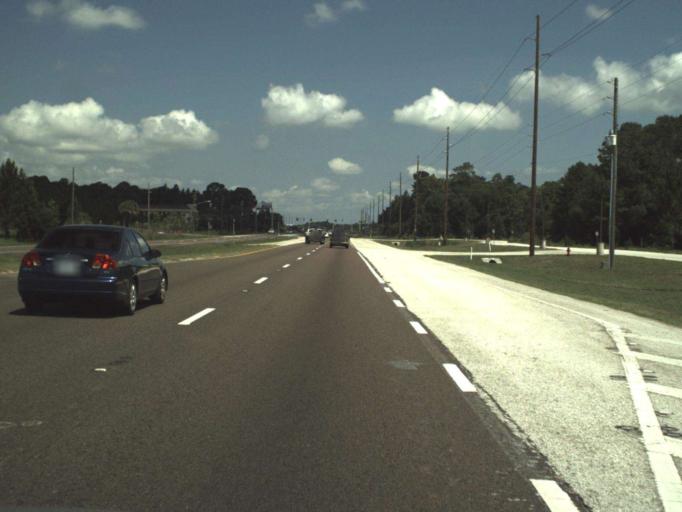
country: US
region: Florida
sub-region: Lake County
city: Mount Dora
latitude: 28.8154
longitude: -81.6288
